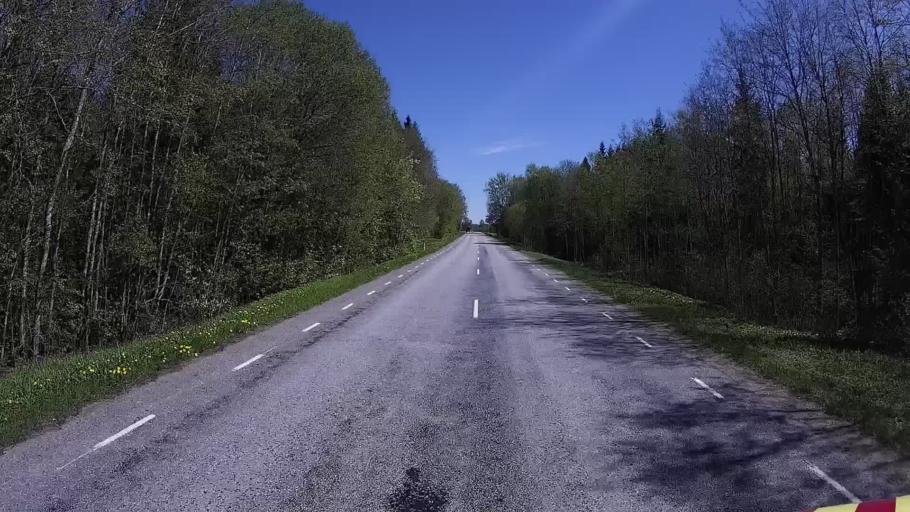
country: EE
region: Raplamaa
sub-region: Kehtna vald
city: Kehtna
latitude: 59.0381
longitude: 25.0434
